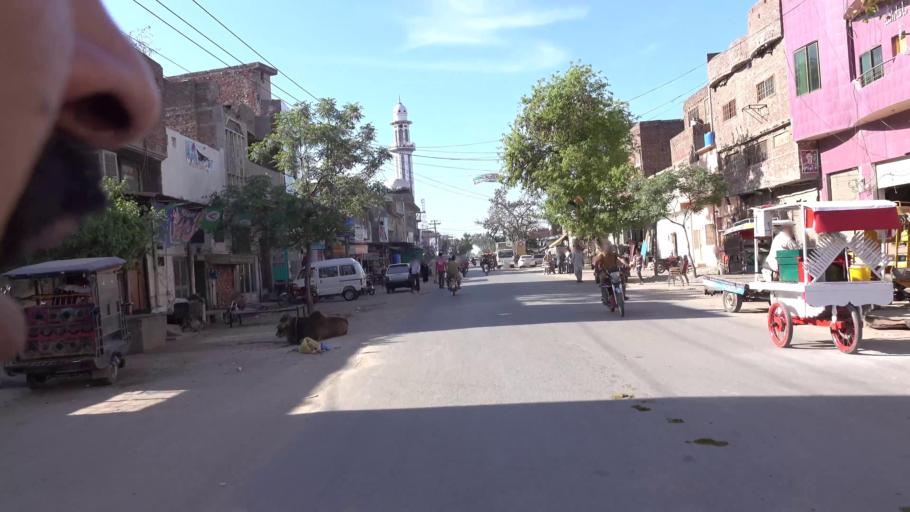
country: PK
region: Punjab
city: Hafizabad
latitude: 32.0749
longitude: 73.6851
